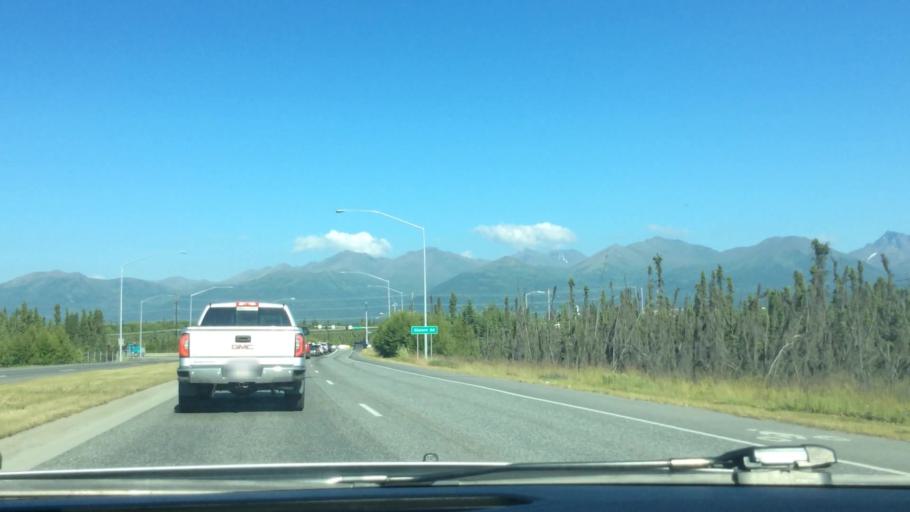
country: US
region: Alaska
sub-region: Anchorage Municipality
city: Anchorage
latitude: 61.1670
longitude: -149.8133
